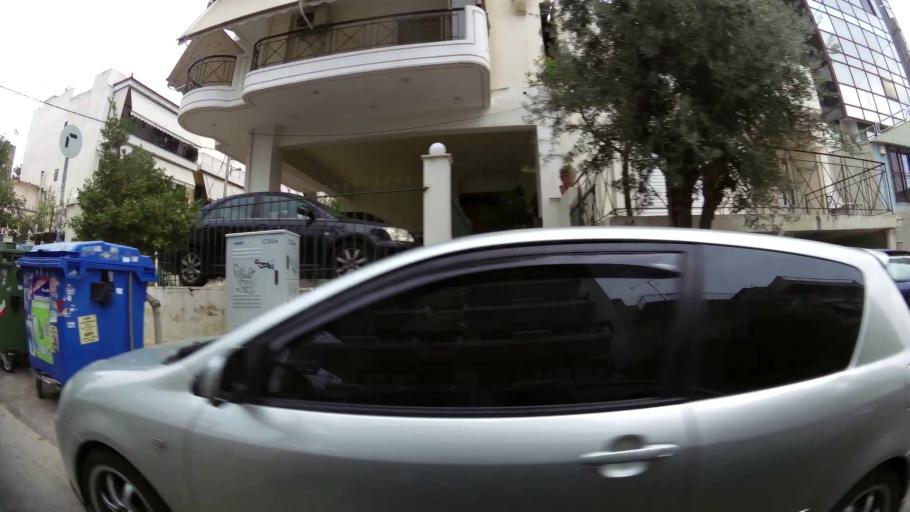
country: GR
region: Attica
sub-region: Nomos Piraios
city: Keratsini
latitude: 37.9773
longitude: 23.6274
